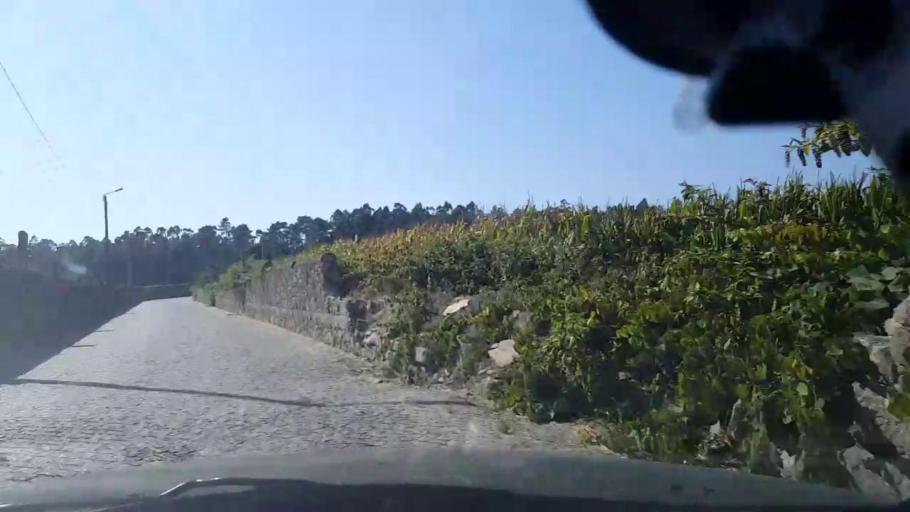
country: PT
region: Porto
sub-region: Povoa de Varzim
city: Pedroso
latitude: 41.4019
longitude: -8.6915
